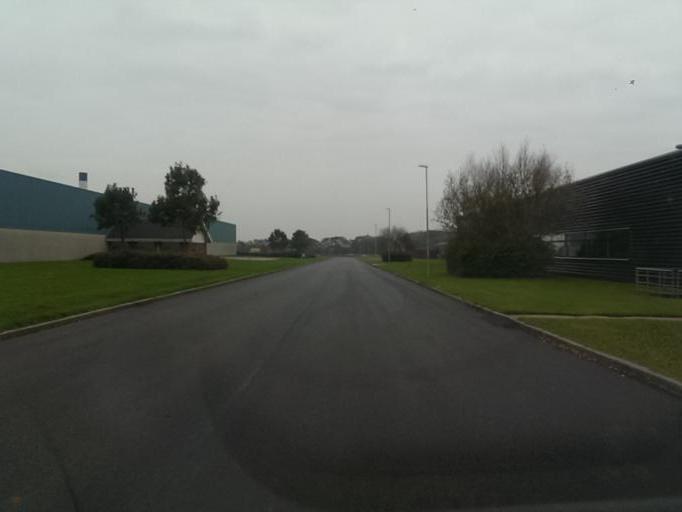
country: DK
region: South Denmark
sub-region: Esbjerg Kommune
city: Esbjerg
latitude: 55.5071
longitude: 8.4770
